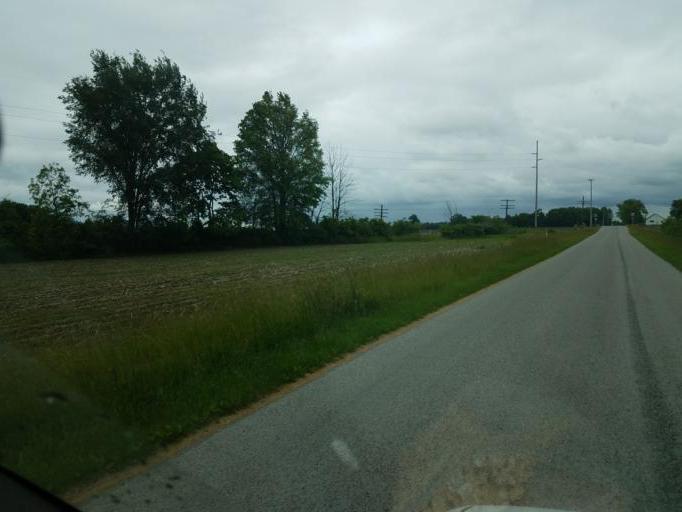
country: US
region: Ohio
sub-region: Morrow County
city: Cardington
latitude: 40.5343
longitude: -82.8769
